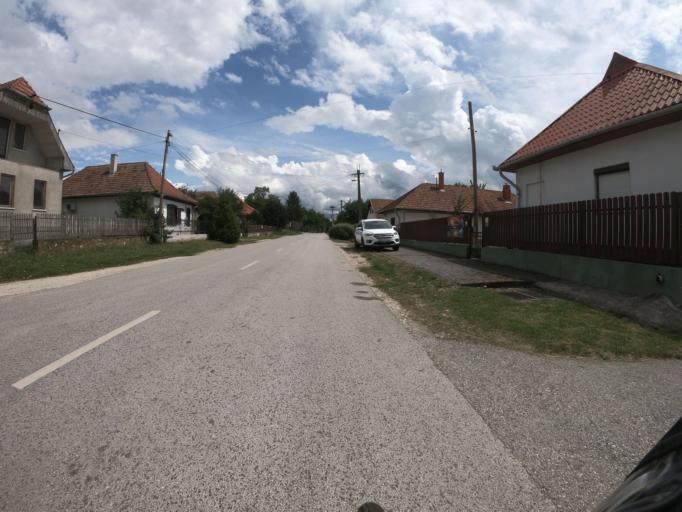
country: HU
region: Jasz-Nagykun-Szolnok
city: Tiszafured
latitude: 47.6893
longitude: 20.8106
